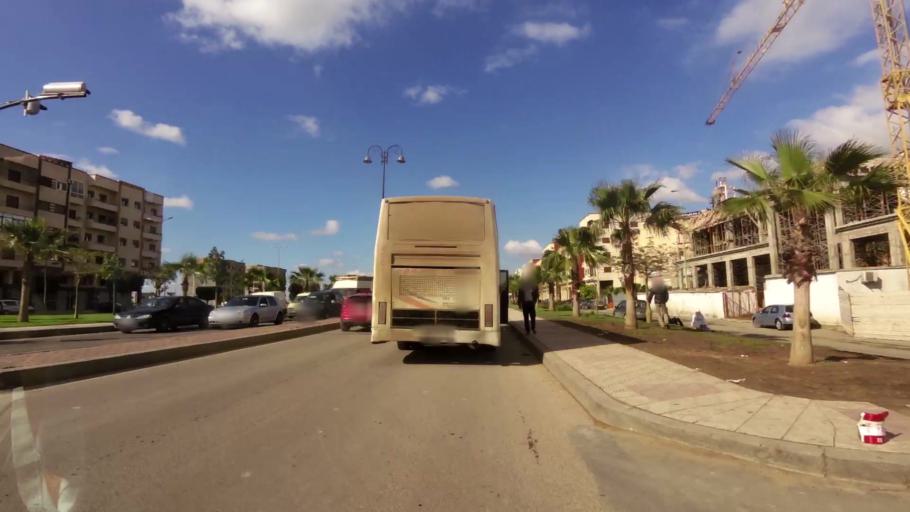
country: MA
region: Chaouia-Ouardigha
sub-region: Settat Province
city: Berrechid
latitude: 33.2758
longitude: -7.5827
